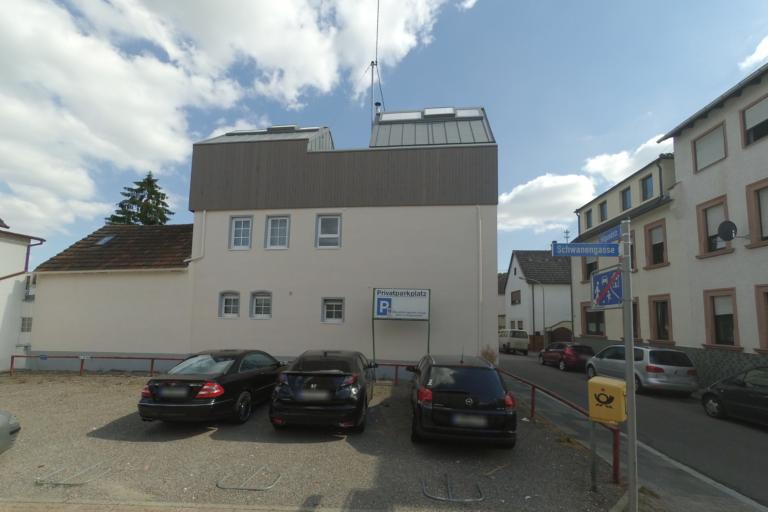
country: DE
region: Rheinland-Pfalz
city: Neuhofen
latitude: 49.4455
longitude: 8.4184
